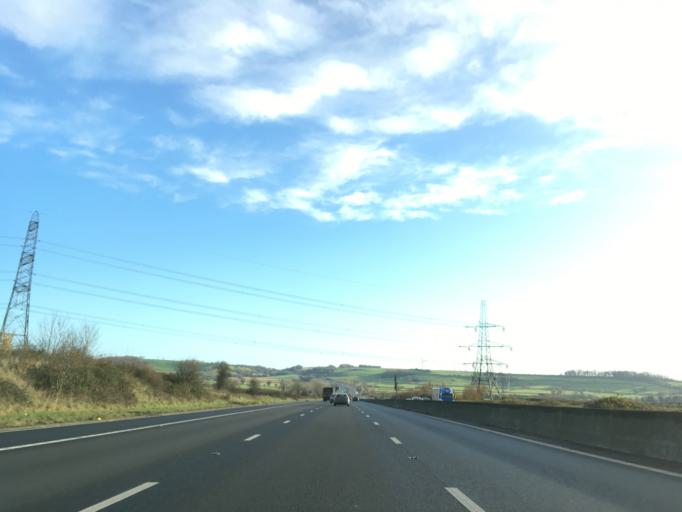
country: GB
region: England
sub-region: South Gloucestershire
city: Hinton
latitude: 51.4981
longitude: -2.4054
